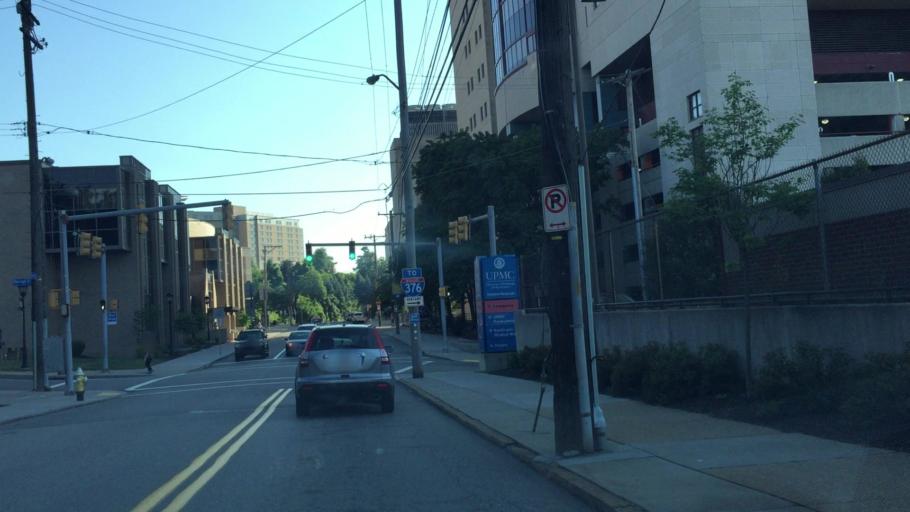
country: US
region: Pennsylvania
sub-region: Allegheny County
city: Bloomfield
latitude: 40.4417
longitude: -79.9631
